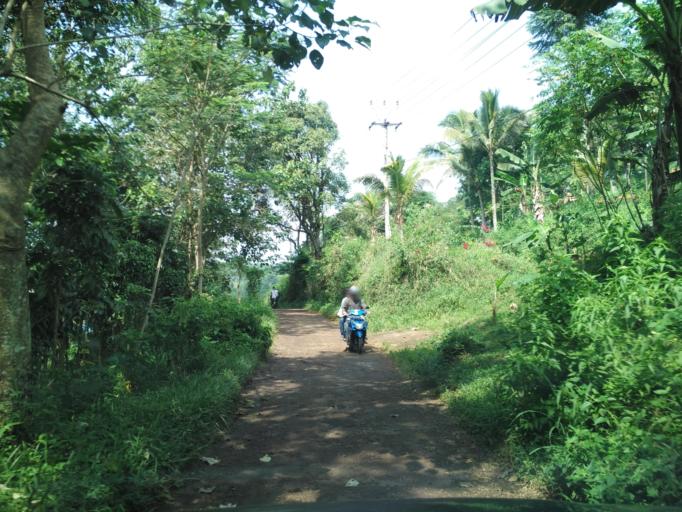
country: ID
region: West Java
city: Ciranjang-hilir
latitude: -6.7953
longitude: 107.1095
